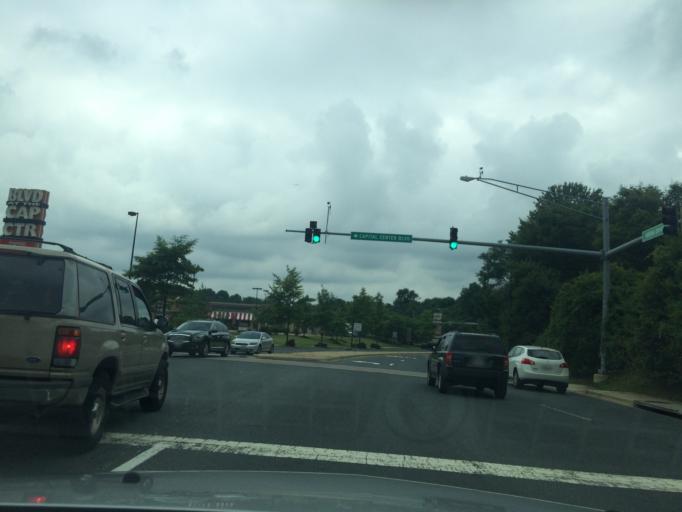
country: US
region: Maryland
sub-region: Prince George's County
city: Lake Arbor
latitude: 38.9048
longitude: -76.8452
